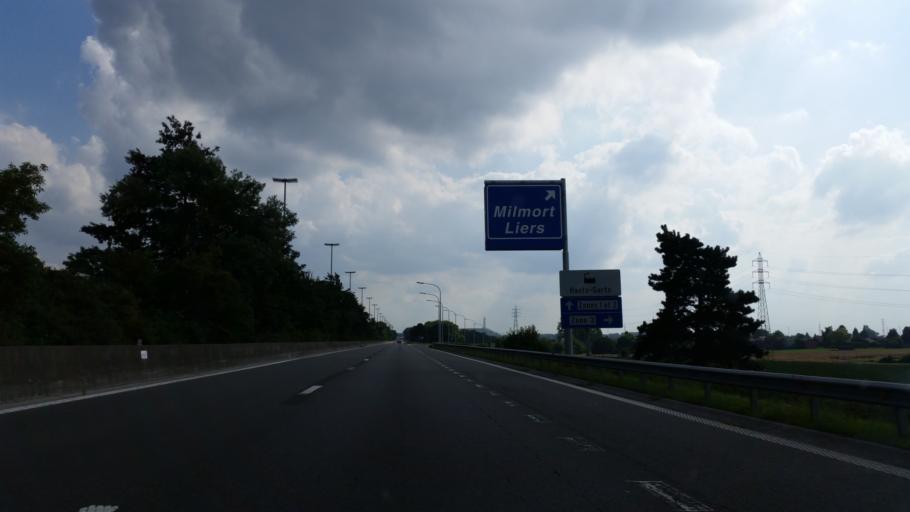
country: BE
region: Wallonia
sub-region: Province de Liege
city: Juprelle
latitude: 50.6950
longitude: 5.5767
